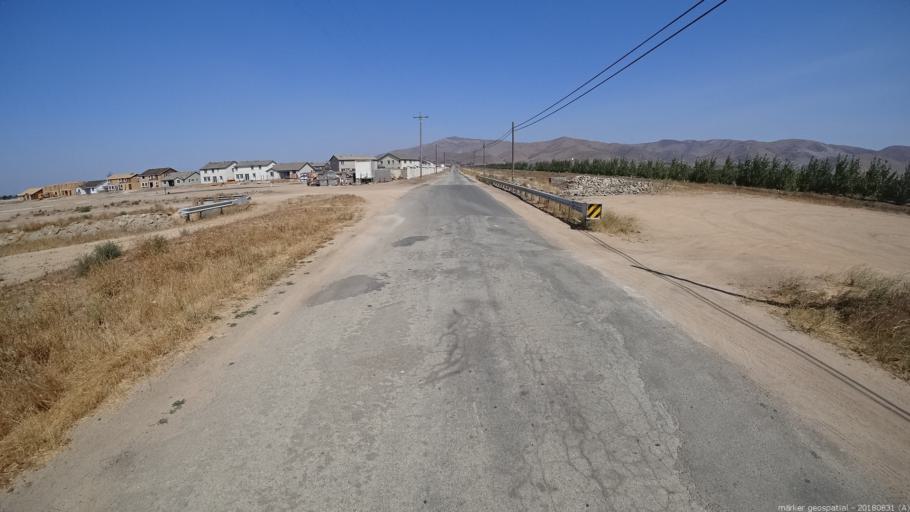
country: US
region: California
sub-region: Monterey County
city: Soledad
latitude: 36.4301
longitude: -121.3121
